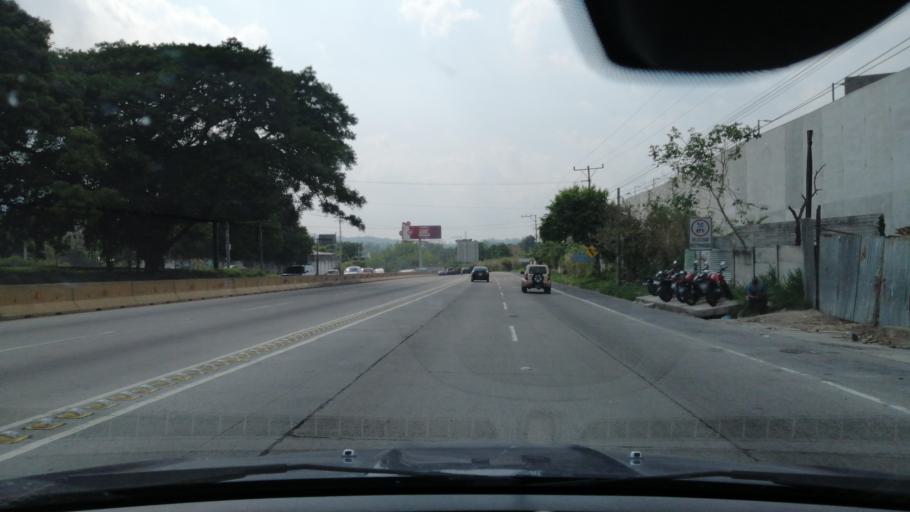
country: SV
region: La Libertad
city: Santa Tecla
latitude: 13.6765
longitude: -89.3048
